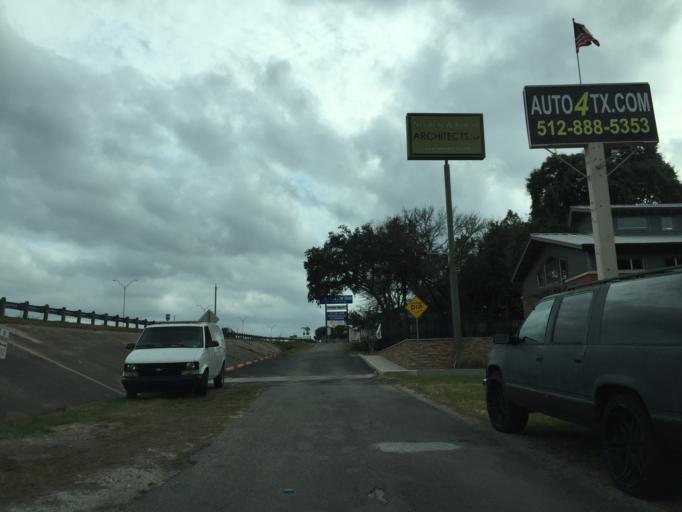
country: US
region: Texas
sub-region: Travis County
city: Wells Branch
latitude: 30.3839
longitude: -97.6740
